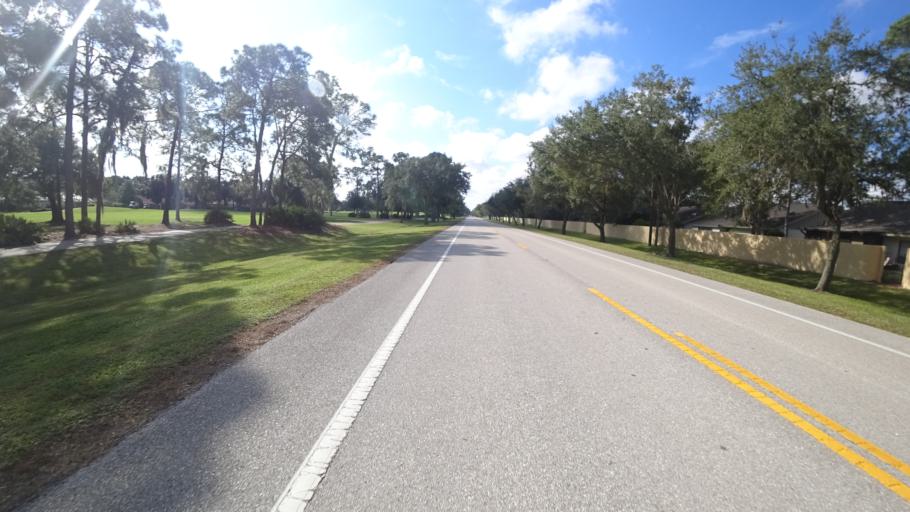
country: US
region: Florida
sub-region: Sarasota County
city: Desoto Lakes
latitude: 27.4020
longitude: -82.4871
